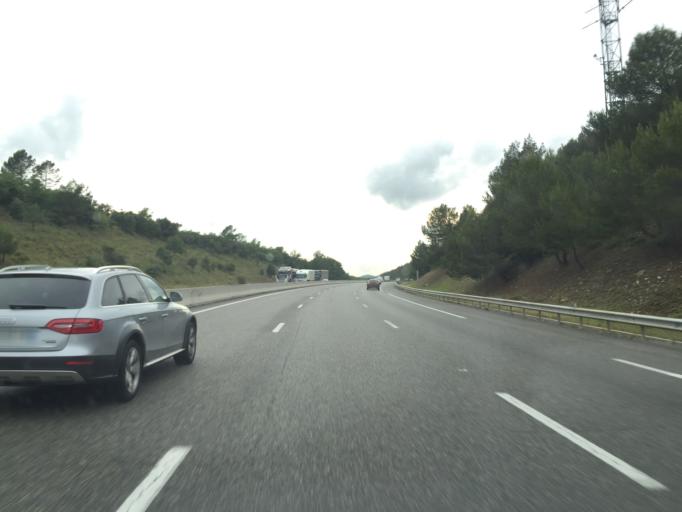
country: FR
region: Provence-Alpes-Cote d'Azur
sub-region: Departement du Var
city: Camps-la-Source
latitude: 43.4112
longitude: 6.1466
